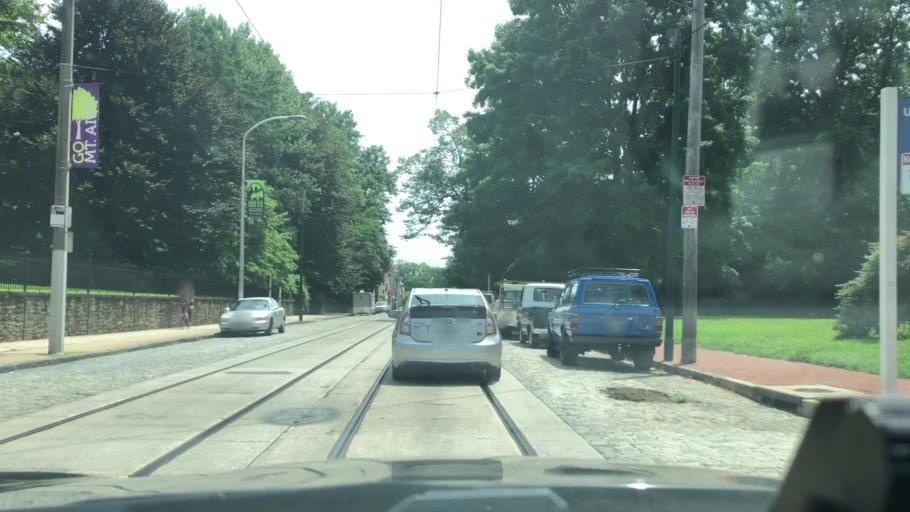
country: US
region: Pennsylvania
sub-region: Montgomery County
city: Wyndmoor
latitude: 40.0474
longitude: -75.1830
